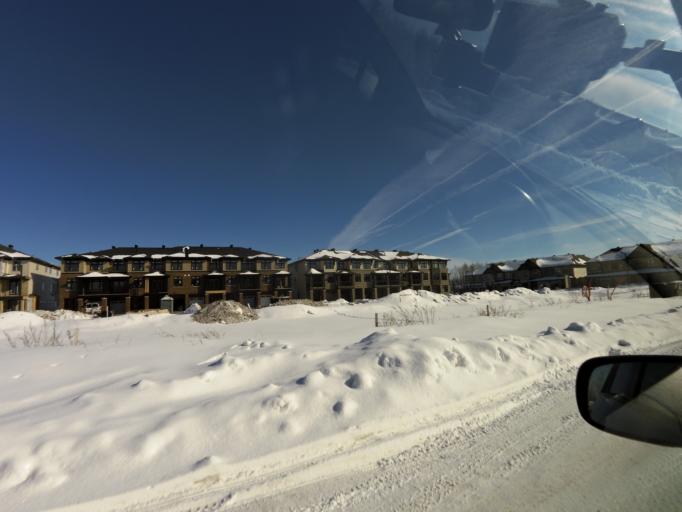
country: CA
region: Ontario
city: Ottawa
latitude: 45.4373
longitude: -75.5126
